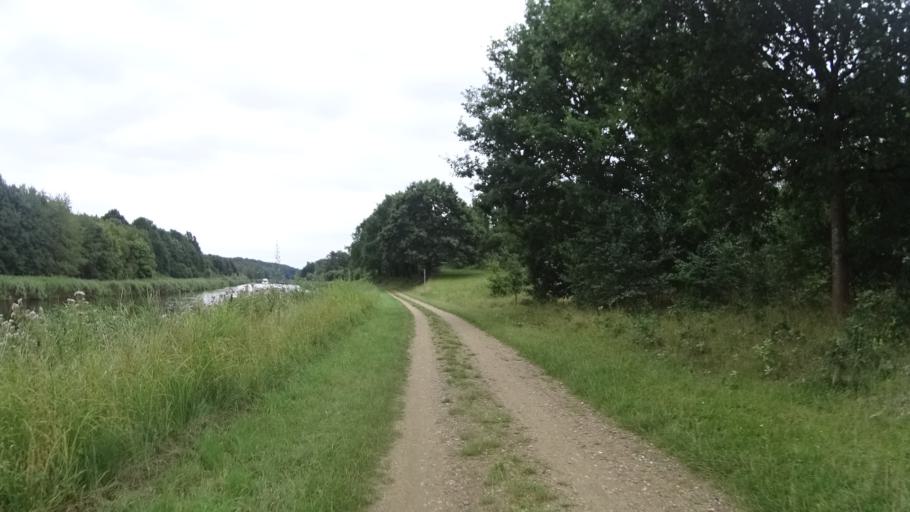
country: DE
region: Schleswig-Holstein
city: Lankau
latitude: 53.6451
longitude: 10.6492
